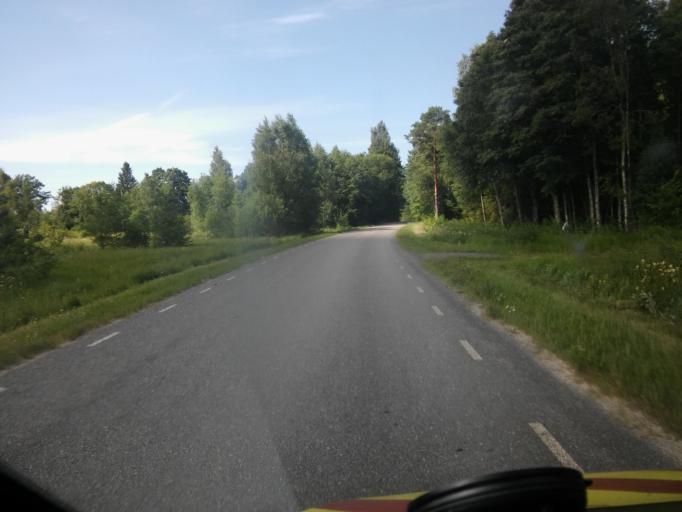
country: EE
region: Paernumaa
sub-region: Sindi linn
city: Sindi
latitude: 58.2504
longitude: 24.7595
